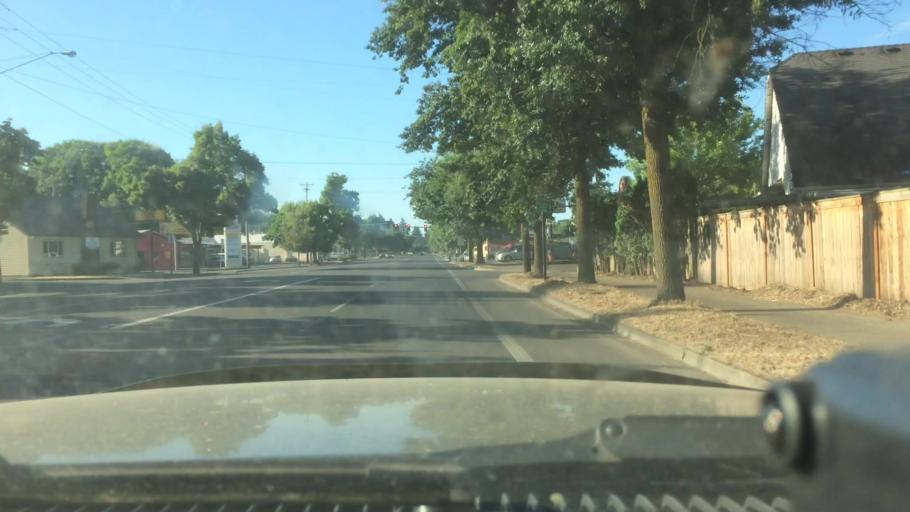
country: US
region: Oregon
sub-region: Lane County
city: Eugene
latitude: 44.0804
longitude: -123.1218
